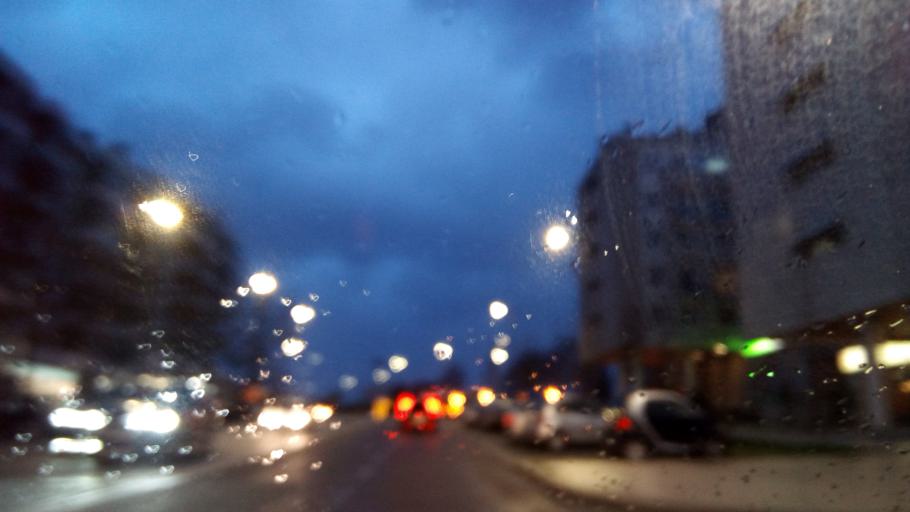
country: PT
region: Viseu
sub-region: Viseu
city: Viseu
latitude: 40.6538
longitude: -7.9144
